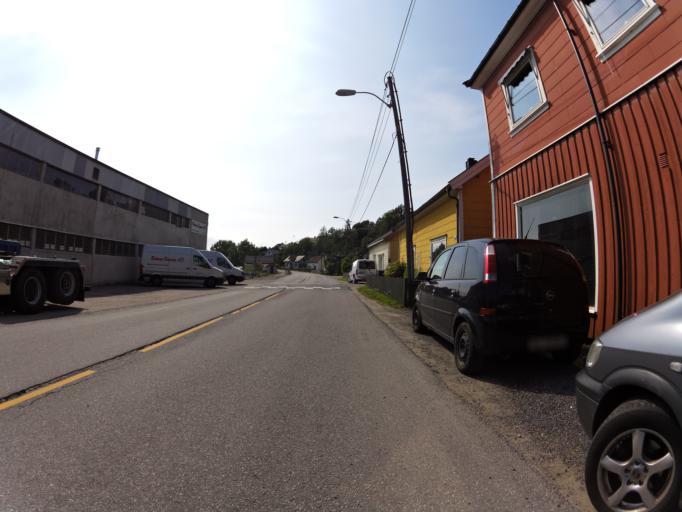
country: NO
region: Ostfold
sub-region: Sarpsborg
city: Sarpsborg
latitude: 59.2677
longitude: 11.0603
